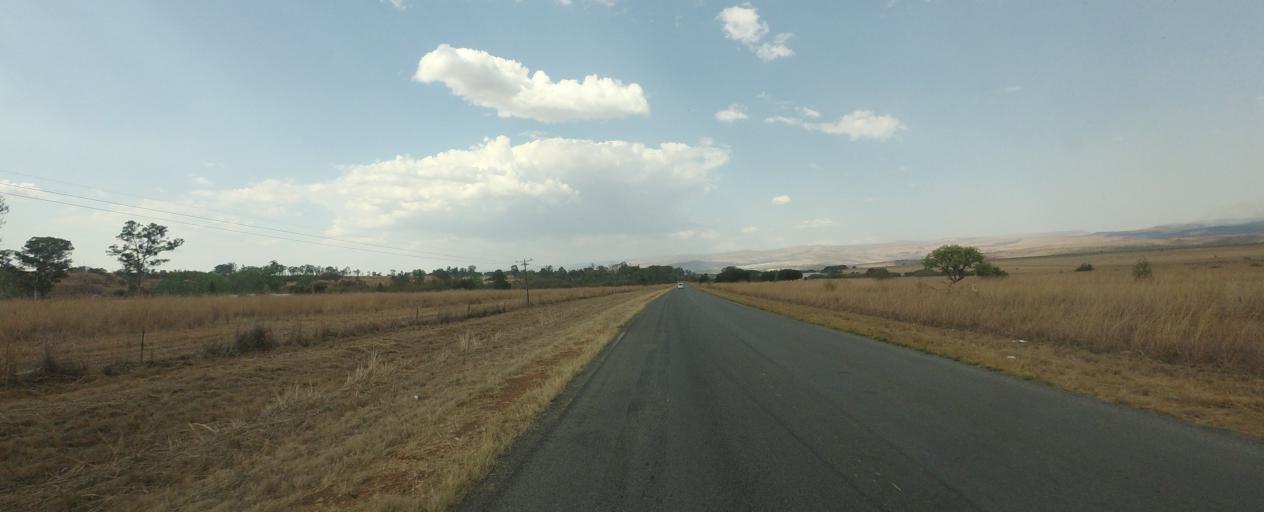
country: ZA
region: Mpumalanga
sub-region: Ehlanzeni District
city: Lydenburg
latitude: -25.1421
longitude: 30.3987
